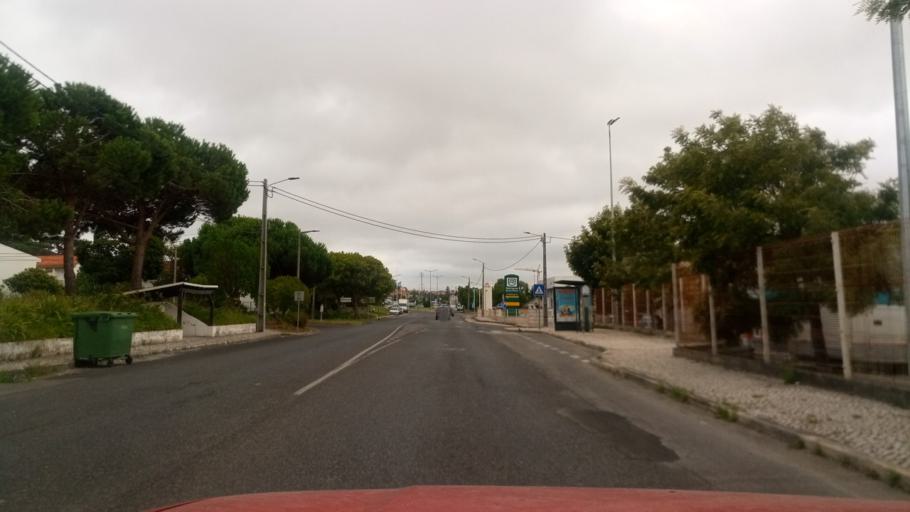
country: PT
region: Leiria
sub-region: Caldas da Rainha
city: Caldas da Rainha
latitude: 39.4237
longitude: -9.1312
